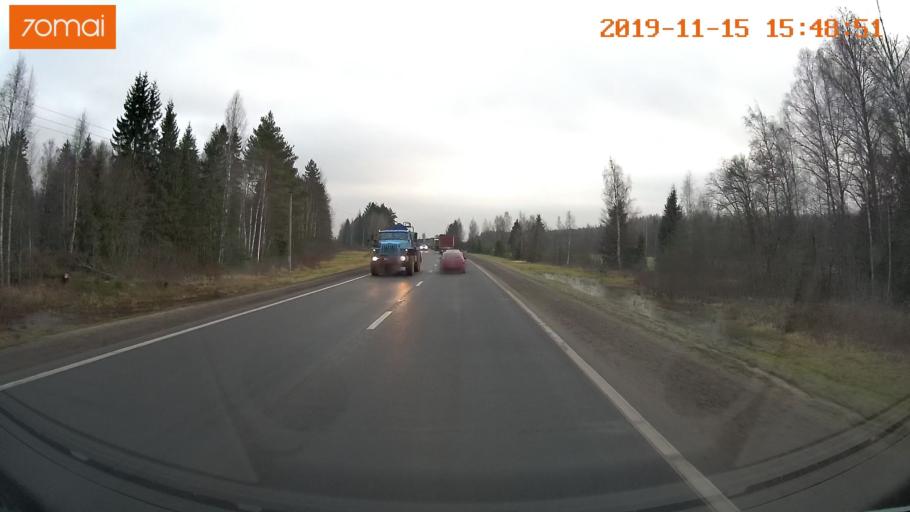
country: RU
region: Jaroslavl
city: Danilov
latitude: 57.9224
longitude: 40.0066
